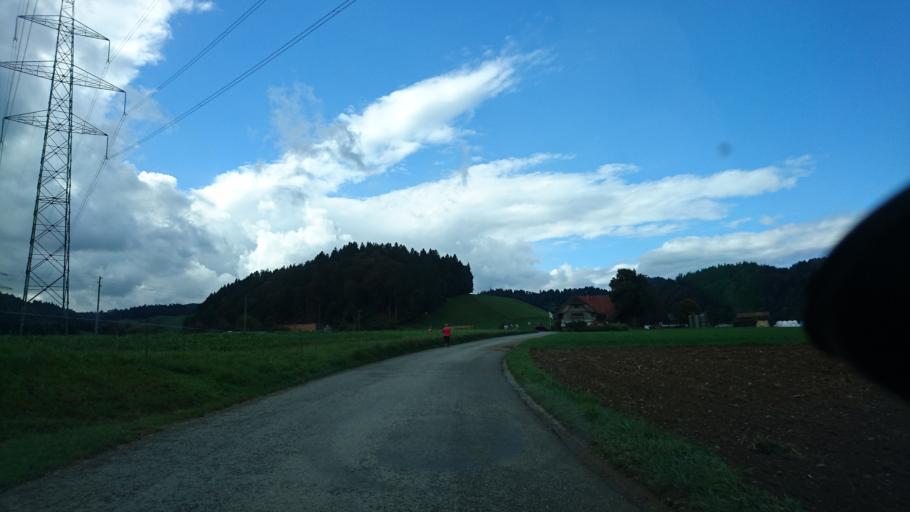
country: CH
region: Bern
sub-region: Emmental District
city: Lutzelfluh
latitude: 47.0013
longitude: 7.6711
